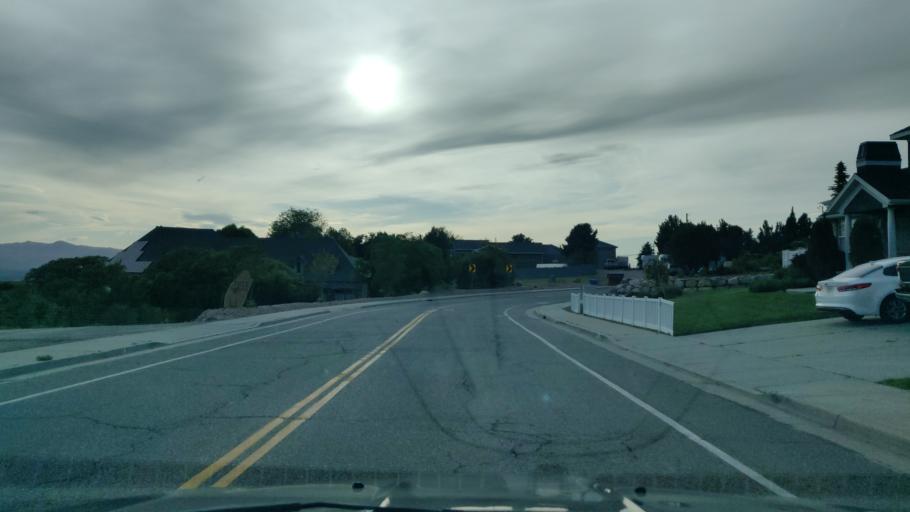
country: US
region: Utah
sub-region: Salt Lake County
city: Cottonwood Heights
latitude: 40.6078
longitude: -111.8094
